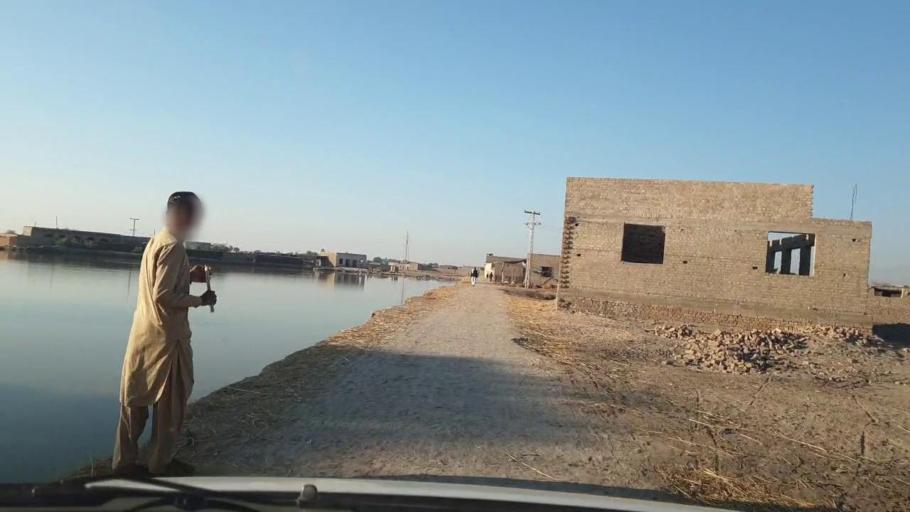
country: PK
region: Sindh
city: Khairpur Nathan Shah
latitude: 27.0449
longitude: 67.7260
